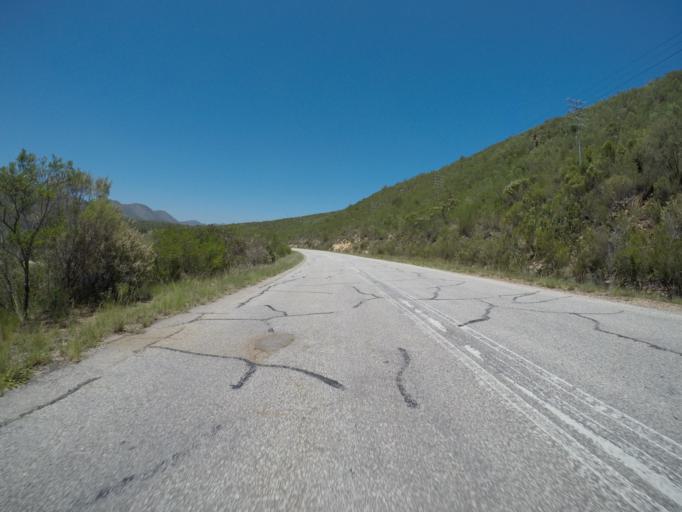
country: ZA
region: Eastern Cape
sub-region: Cacadu District Municipality
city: Kareedouw
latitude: -33.8848
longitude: 24.0704
